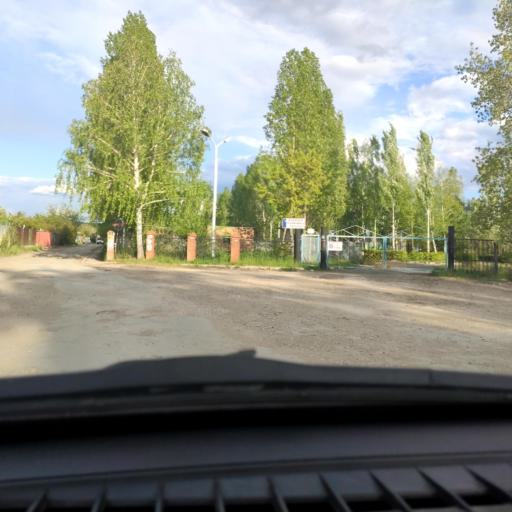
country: RU
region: Samara
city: Zhigulevsk
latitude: 53.4501
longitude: 49.5348
